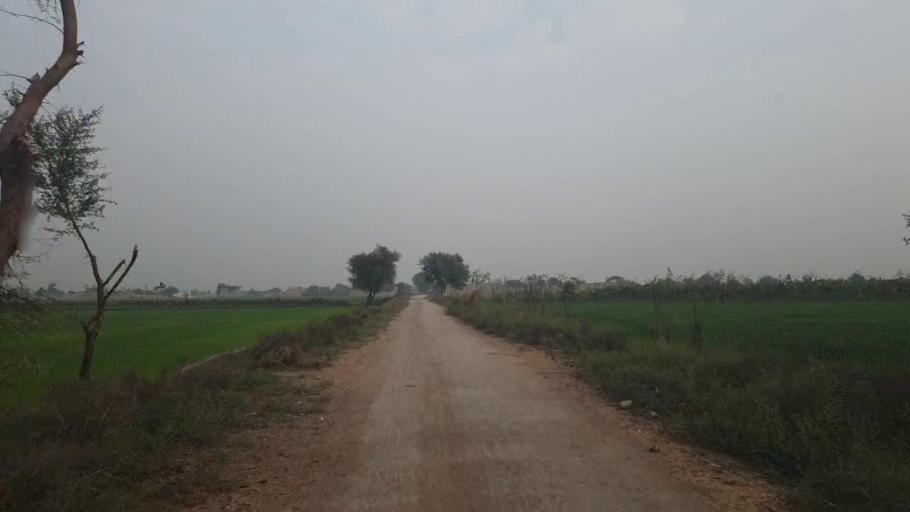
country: PK
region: Sindh
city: Berani
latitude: 25.7969
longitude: 68.7474
